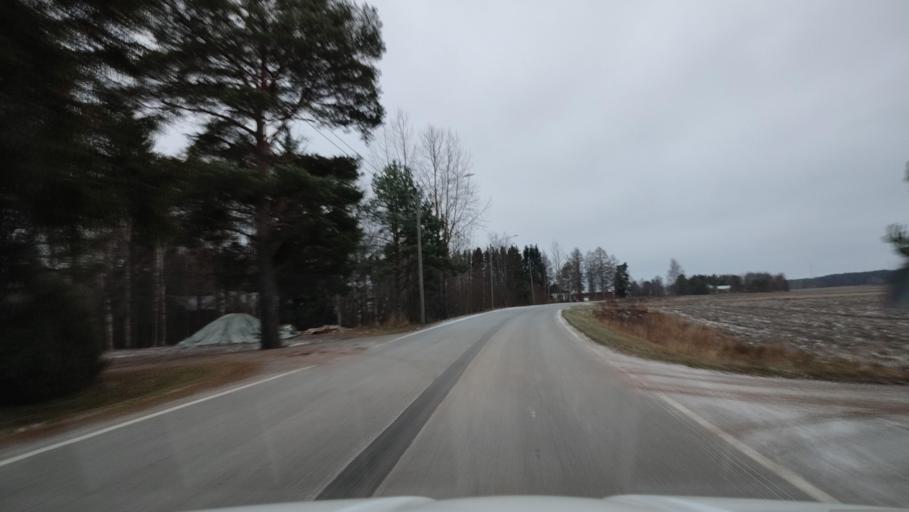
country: FI
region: Southern Ostrobothnia
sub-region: Suupohja
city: Karijoki
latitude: 62.2455
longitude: 21.6704
